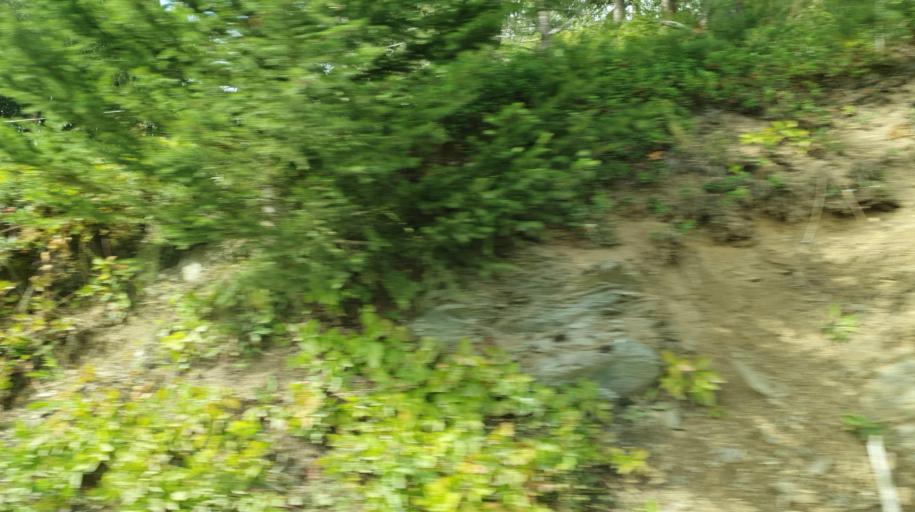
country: NO
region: Nord-Trondelag
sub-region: Levanger
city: Skogn
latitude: 63.5983
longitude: 11.2711
